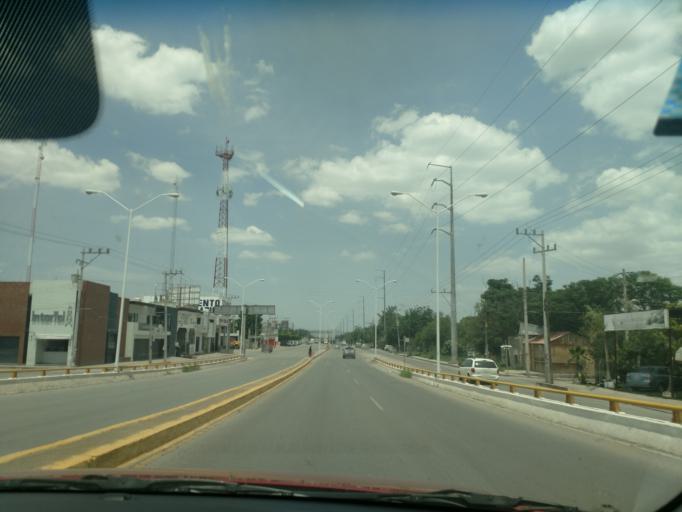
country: MX
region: San Luis Potosi
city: Rio Verde
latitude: 21.9231
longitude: -99.9913
